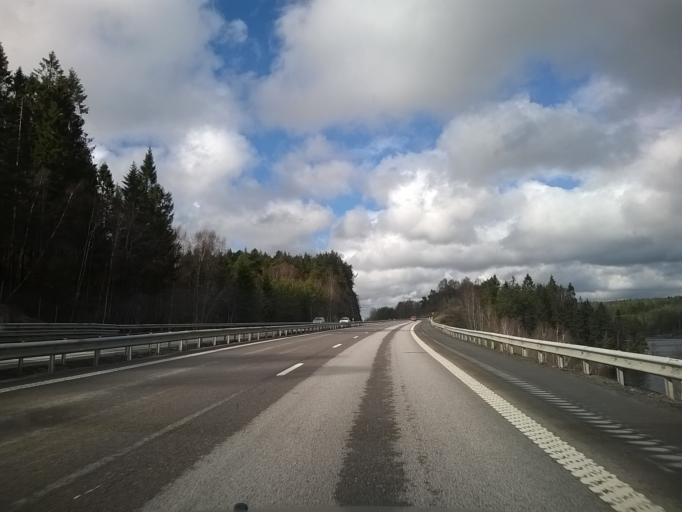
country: SE
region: Halland
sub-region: Kungsbacka Kommun
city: Fjaeras kyrkby
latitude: 57.3917
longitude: 12.1890
